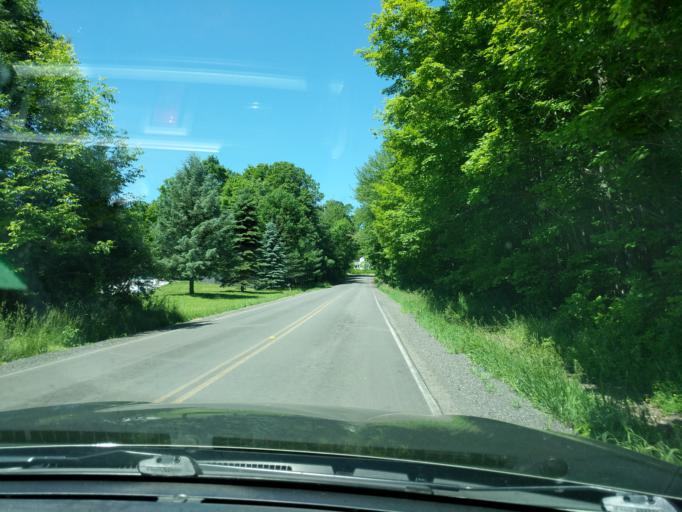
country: US
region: New York
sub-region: Tompkins County
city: East Ithaca
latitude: 42.3683
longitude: -76.4124
